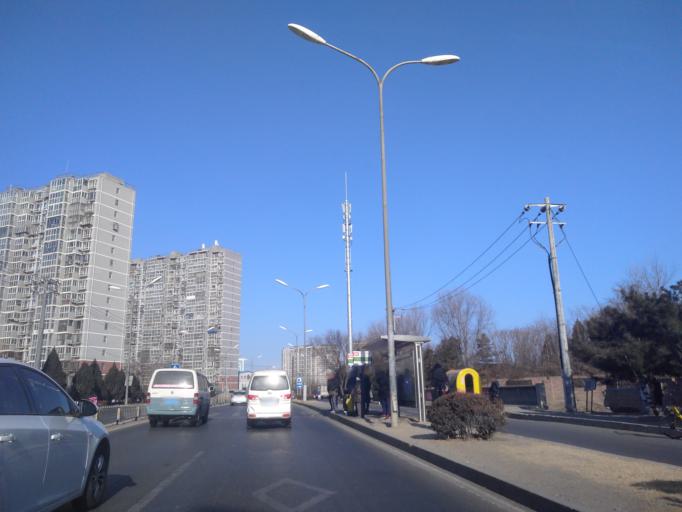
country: CN
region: Beijing
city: Jiugong
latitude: 39.8279
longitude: 116.4717
